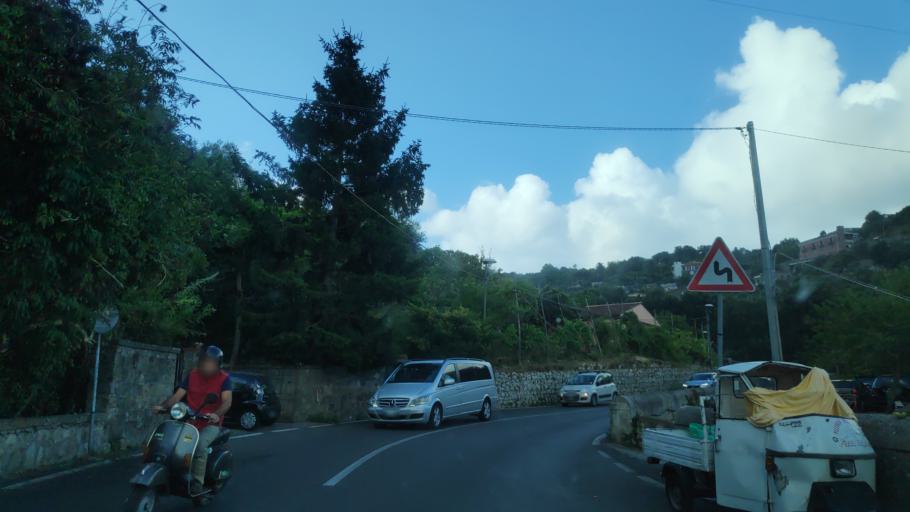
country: IT
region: Campania
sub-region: Provincia di Napoli
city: Piano di Sorrento
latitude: 40.6230
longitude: 14.4239
